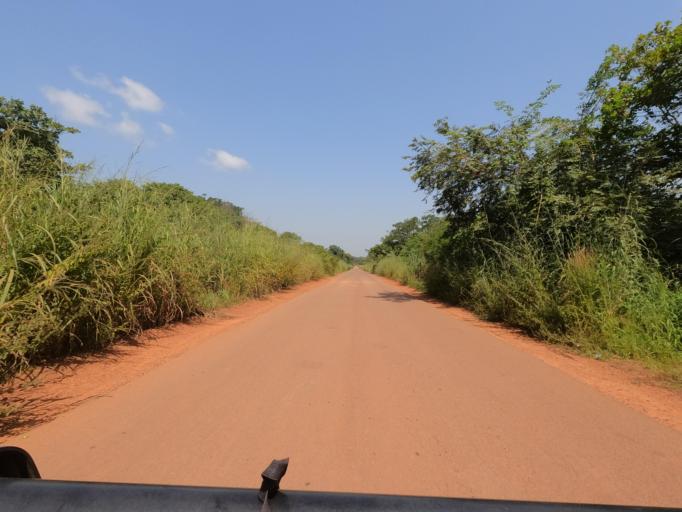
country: GW
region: Oio
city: Bissora
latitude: 12.3444
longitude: -15.7630
